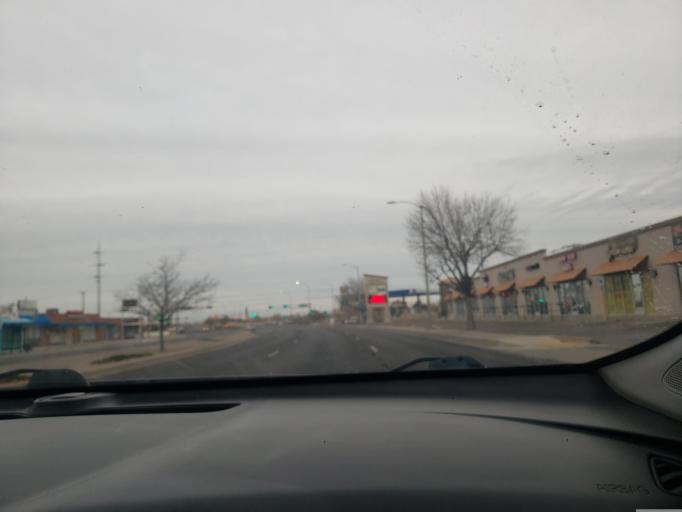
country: US
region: New Mexico
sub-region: Bernalillo County
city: Albuquerque
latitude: 35.1006
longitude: -106.5863
